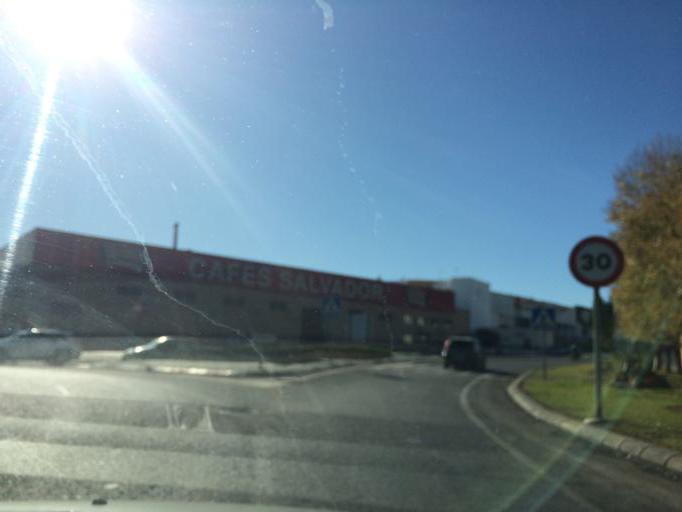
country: ES
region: Andalusia
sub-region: Provincia de Almeria
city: Huercal de Almeria
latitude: 36.8730
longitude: -2.4414
